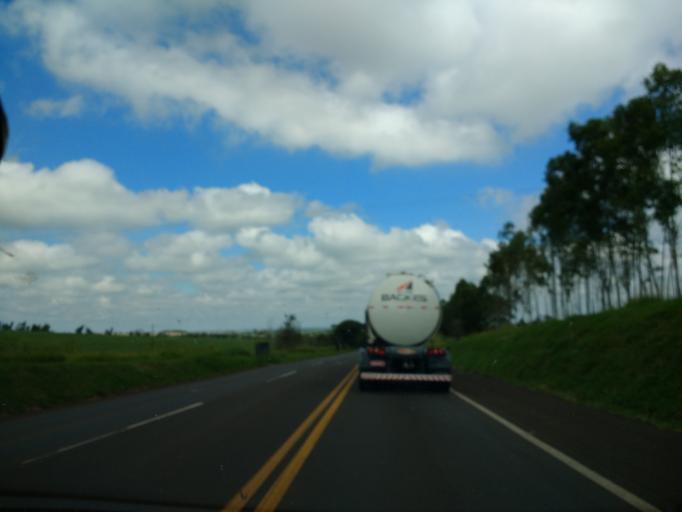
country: BR
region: Parana
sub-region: Cruzeiro Do Oeste
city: Cruzeiro do Oeste
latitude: -23.7834
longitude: -53.0259
